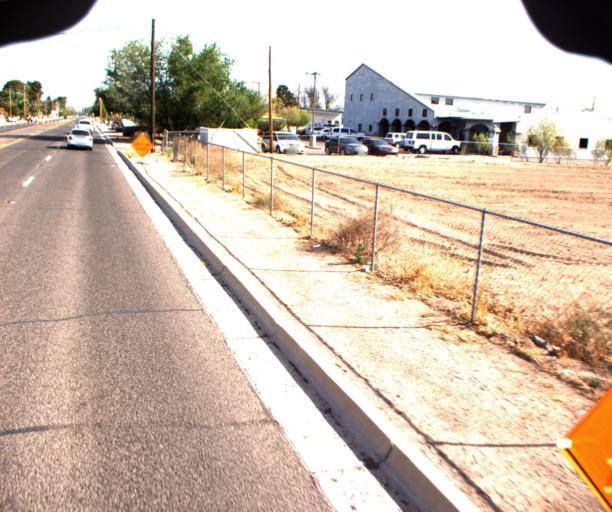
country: US
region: Arizona
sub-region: Graham County
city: Safford
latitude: 32.8195
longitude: -109.7076
